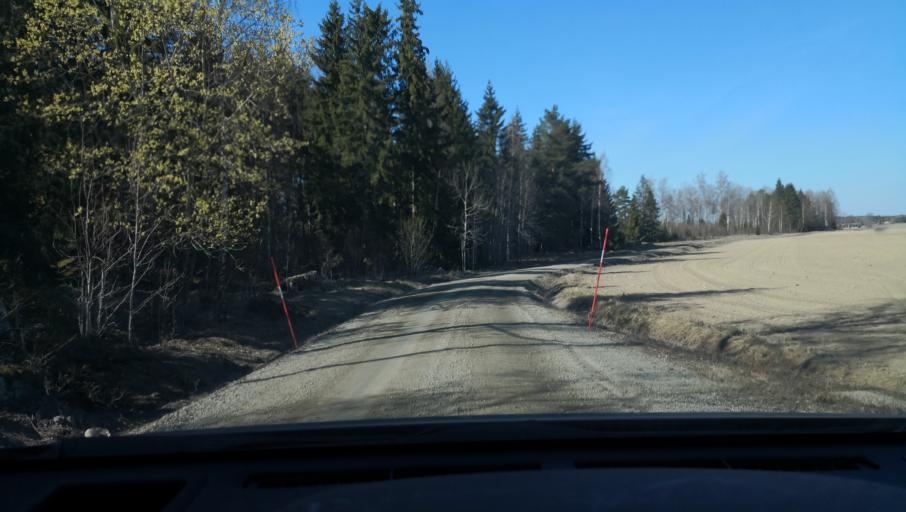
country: SE
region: Vaestmanland
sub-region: Sala Kommun
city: Sala
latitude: 59.8862
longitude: 16.5274
